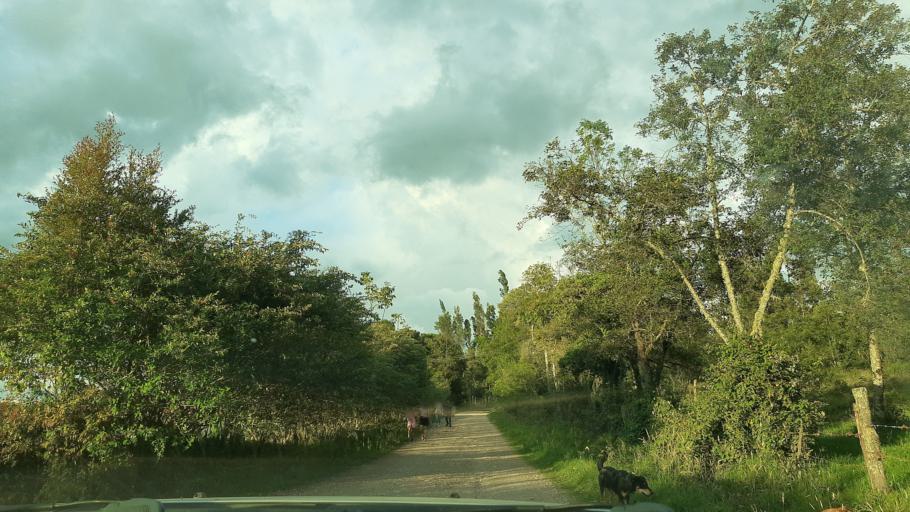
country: CO
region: Boyaca
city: La Capilla
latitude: 5.7108
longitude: -73.4802
